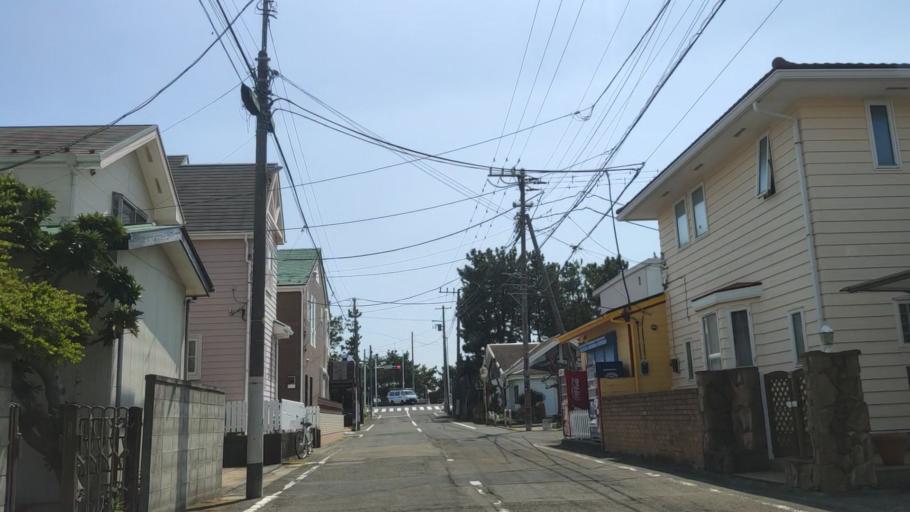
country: JP
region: Kanagawa
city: Hiratsuka
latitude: 35.3158
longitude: 139.3399
